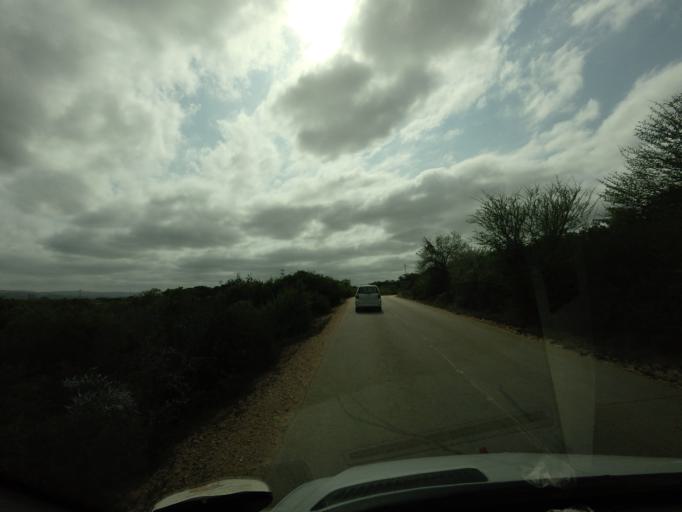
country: ZA
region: Eastern Cape
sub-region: Cacadu District Municipality
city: Kirkwood
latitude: -33.4436
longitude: 25.7441
